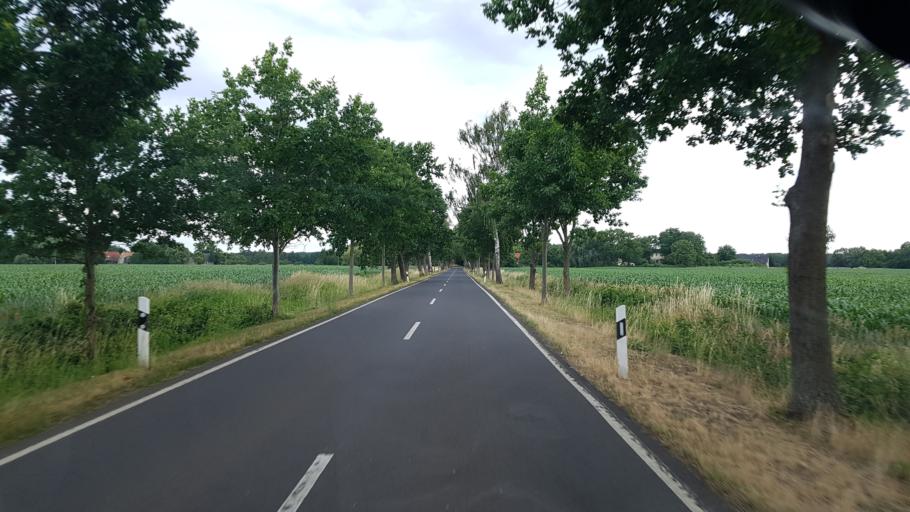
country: DE
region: Brandenburg
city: Kasel-Golzig
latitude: 51.9638
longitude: 13.6740
